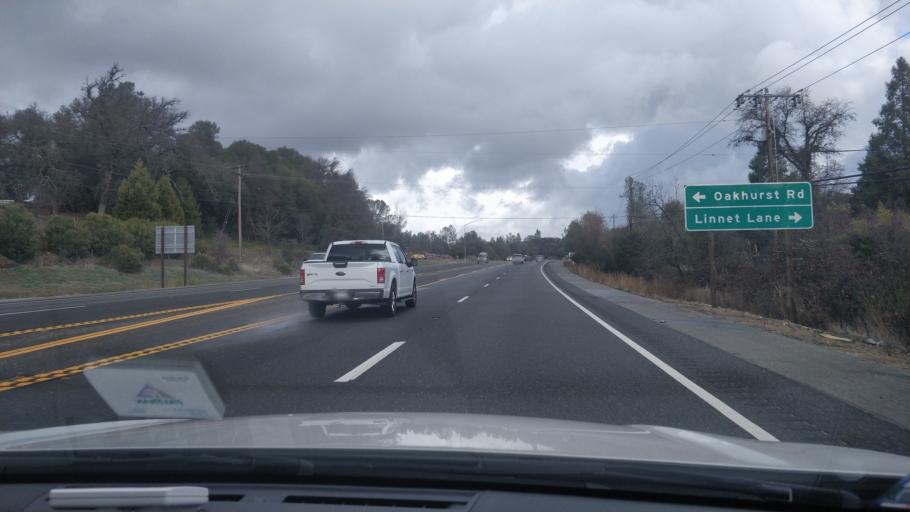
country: US
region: California
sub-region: Nevada County
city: Lake of the Pines
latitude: 39.0122
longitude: -121.1040
